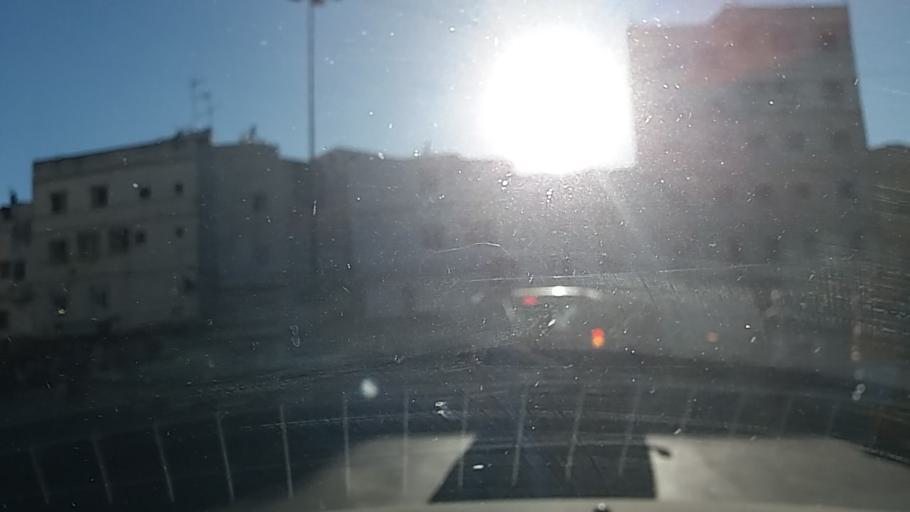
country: MA
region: Tanger-Tetouan
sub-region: Tanger-Assilah
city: Tangier
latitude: 35.7537
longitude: -5.8199
